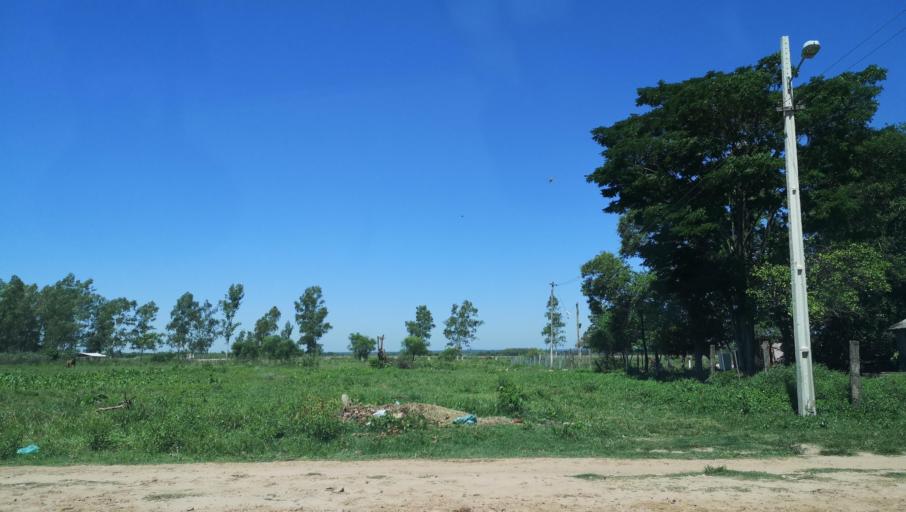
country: PY
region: Caaguazu
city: Carayao
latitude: -25.1960
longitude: -56.4059
